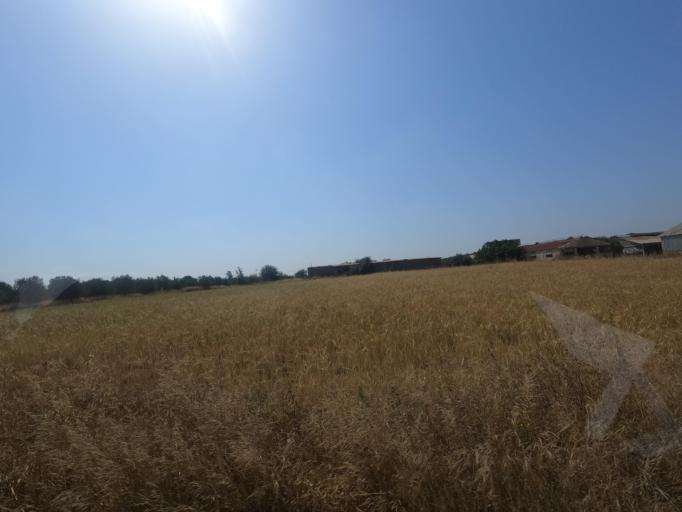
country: CY
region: Ammochostos
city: Avgorou
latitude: 35.0440
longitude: 33.8506
